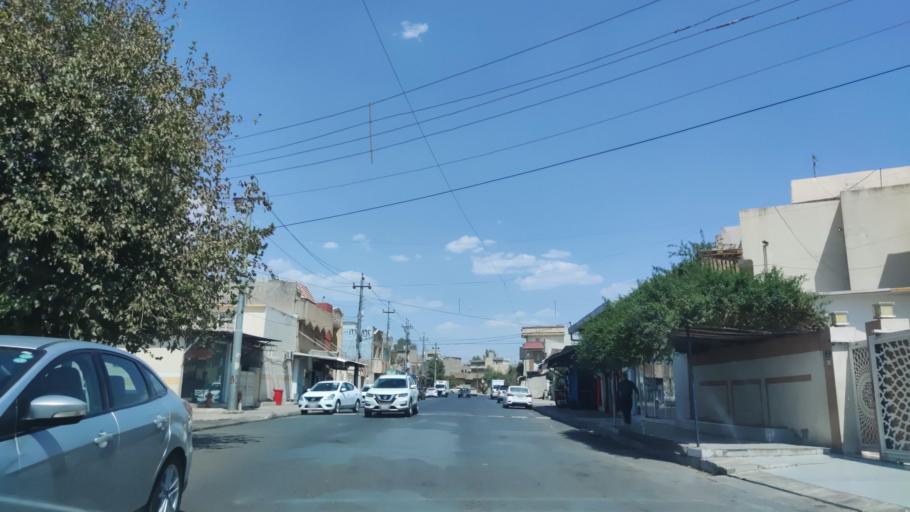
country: IQ
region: Arbil
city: Erbil
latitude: 36.1950
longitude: 44.0205
